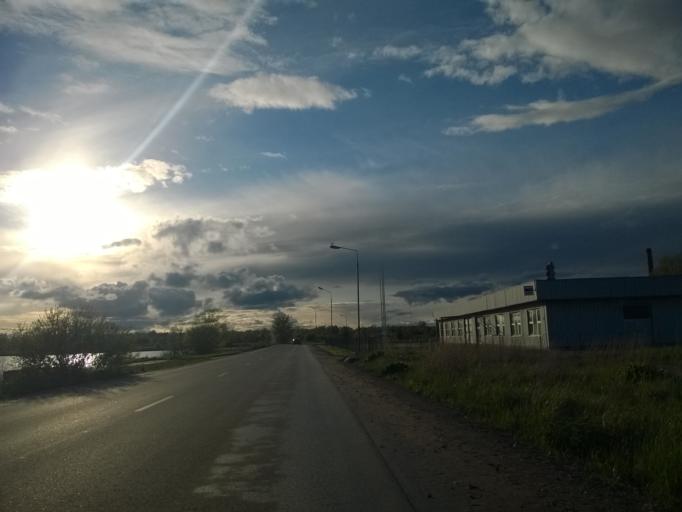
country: LV
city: Tireli
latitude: 56.9347
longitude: 23.6052
